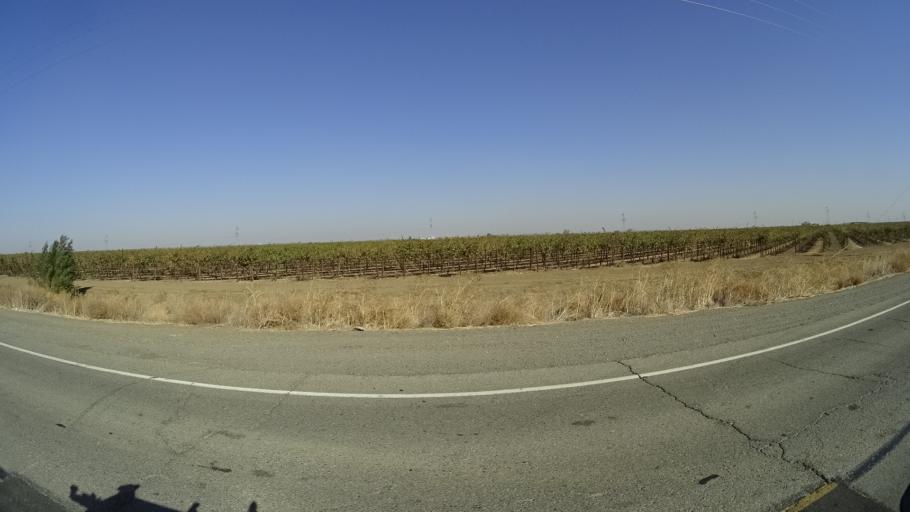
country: US
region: California
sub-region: Yolo County
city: Esparto
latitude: 38.7255
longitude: -121.9715
